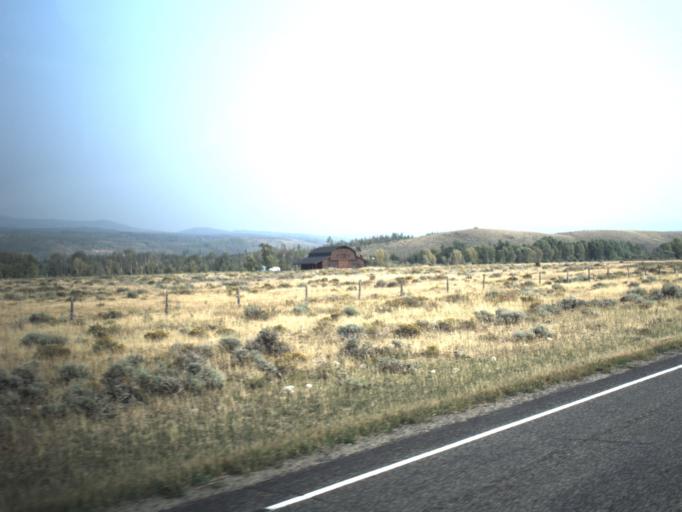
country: US
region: Wyoming
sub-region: Uinta County
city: Evanston
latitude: 40.9921
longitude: -110.8619
